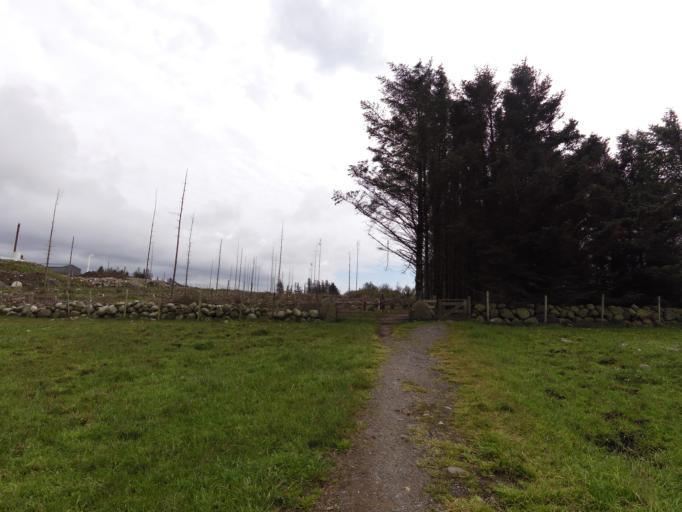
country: NO
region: Rogaland
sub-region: Ha
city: Naerbo
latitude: 58.6317
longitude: 5.5934
